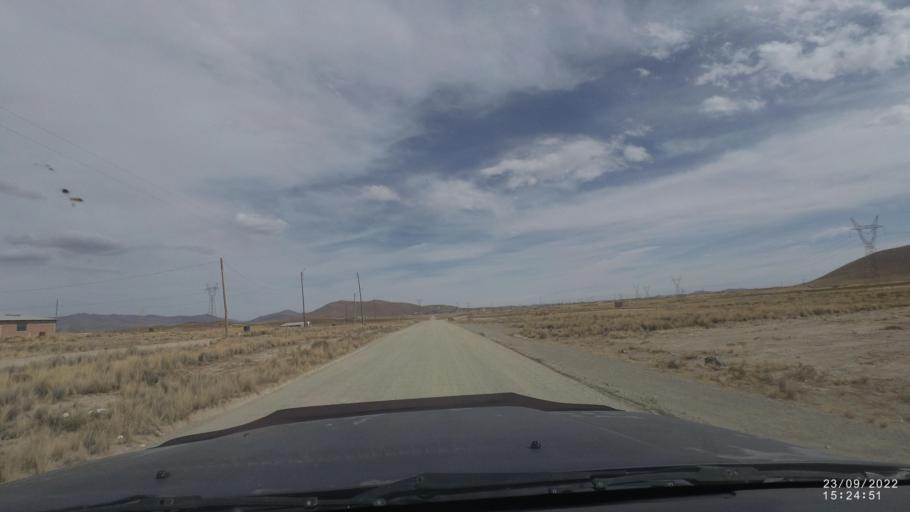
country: BO
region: Oruro
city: Oruro
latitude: -17.9390
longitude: -67.0403
